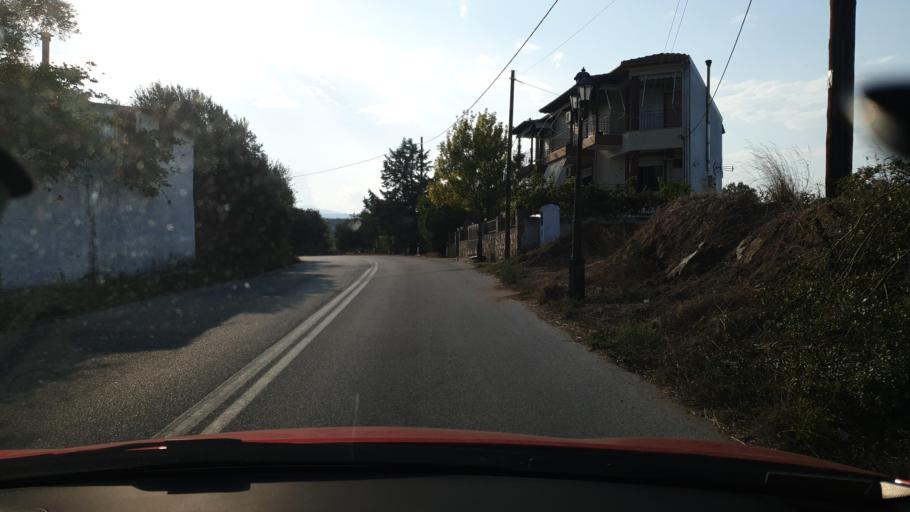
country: GR
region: Thessaly
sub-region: Nomos Magnisias
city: Pteleos
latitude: 39.0096
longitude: 22.9562
